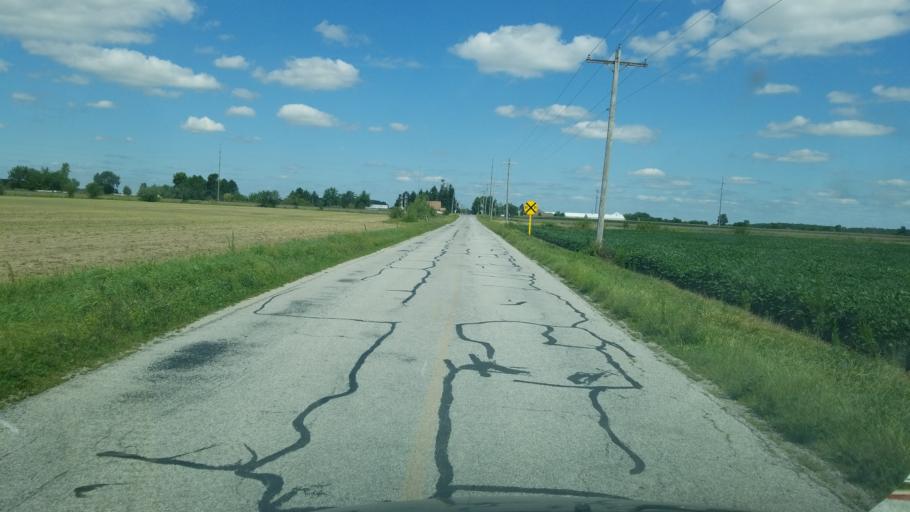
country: US
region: Ohio
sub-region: Fulton County
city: Swanton
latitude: 41.5773
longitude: -83.9408
